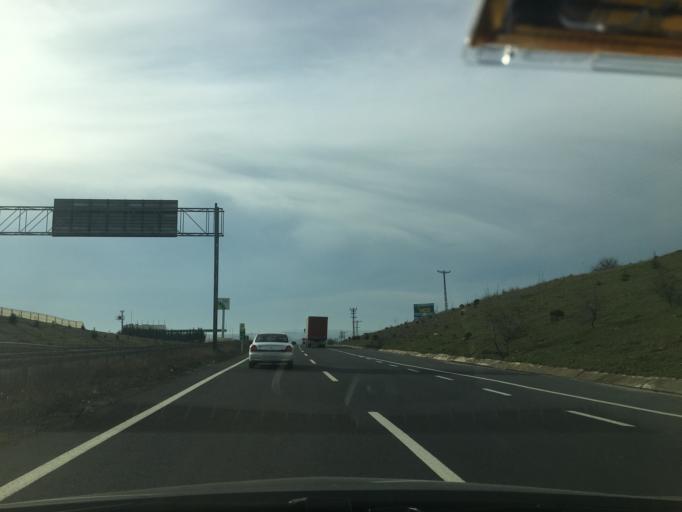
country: TR
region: Istanbul
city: Buyukcavuslu
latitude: 41.2616
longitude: 28.0357
